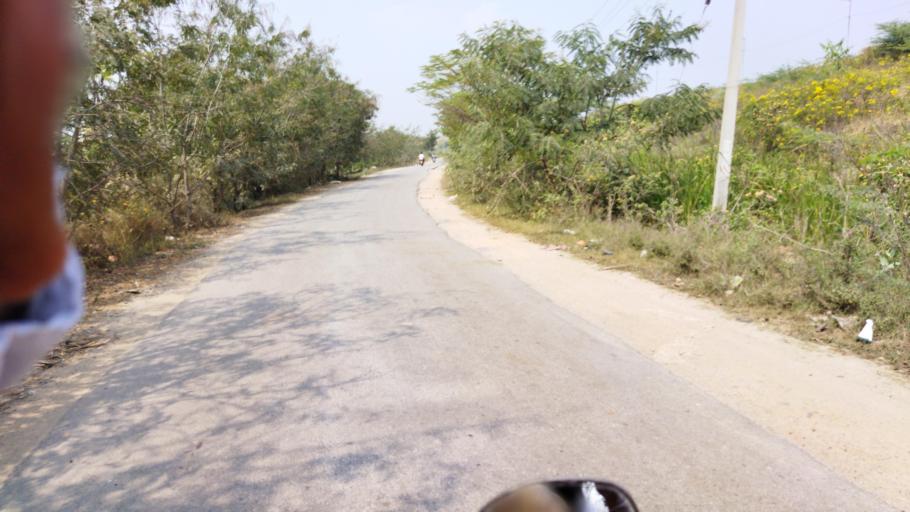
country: IN
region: Telangana
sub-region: Nalgonda
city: Nalgonda
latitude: 17.0737
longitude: 79.3154
